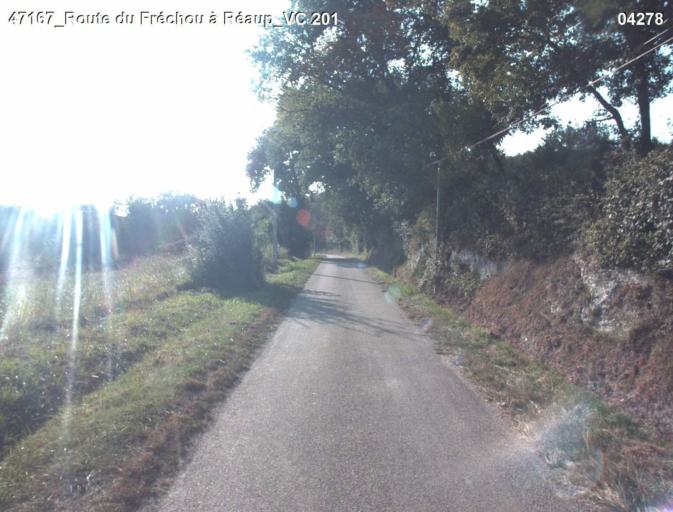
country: FR
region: Aquitaine
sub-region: Departement du Lot-et-Garonne
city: Mezin
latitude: 44.0730
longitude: 0.2648
